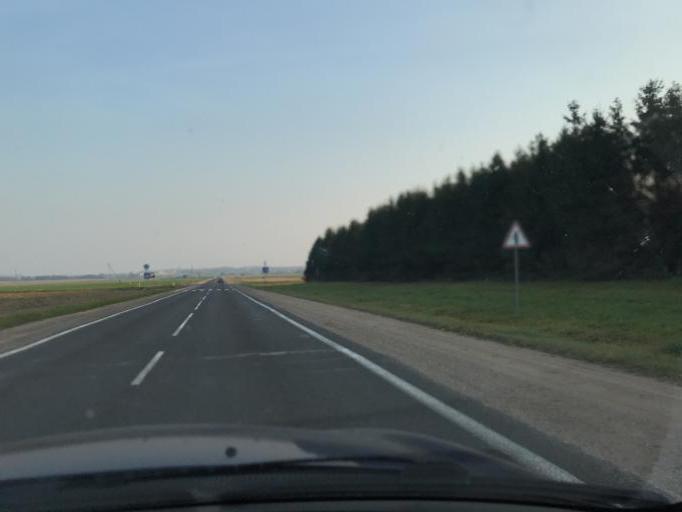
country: BY
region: Grodnenskaya
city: Karelichy
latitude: 53.5544
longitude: 26.1593
